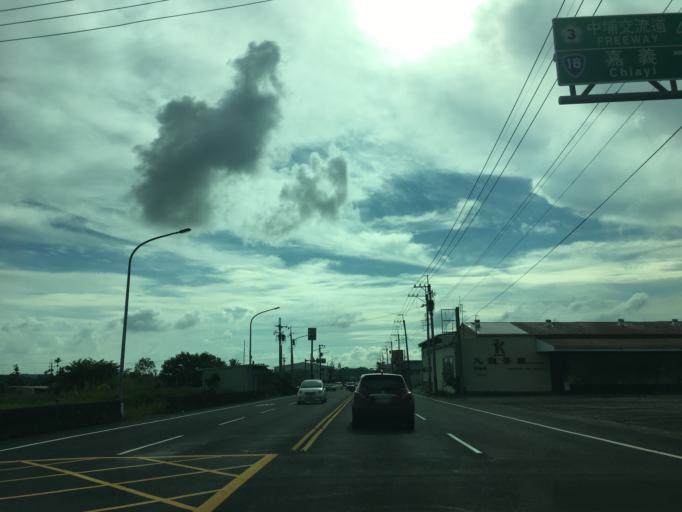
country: TW
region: Taiwan
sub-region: Chiayi
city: Jiayi Shi
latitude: 23.4419
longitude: 120.5241
